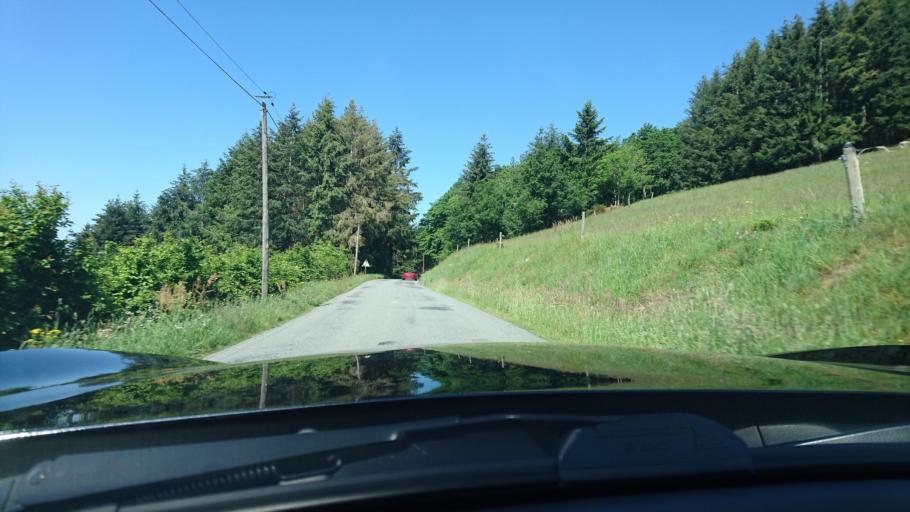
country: FR
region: Rhone-Alpes
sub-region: Departement de la Loire
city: Violay
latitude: 45.8658
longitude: 4.3490
